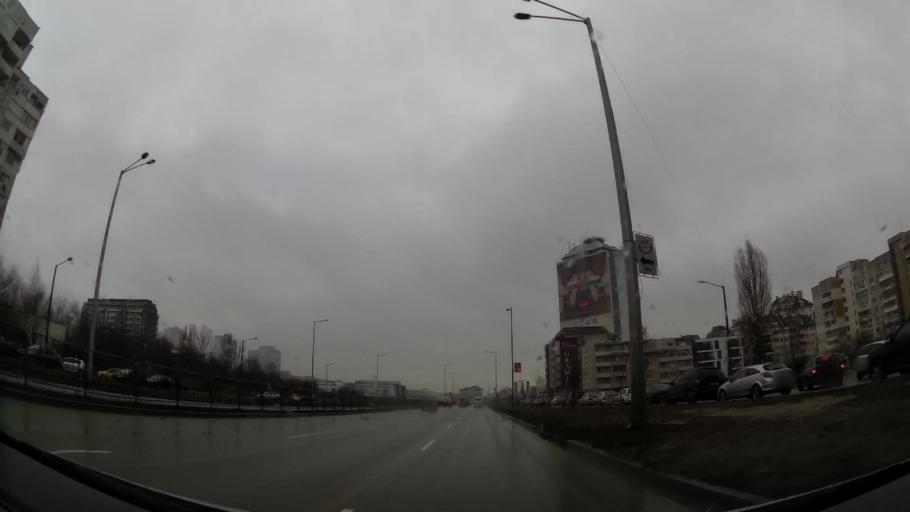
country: BG
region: Sofia-Capital
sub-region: Stolichna Obshtina
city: Sofia
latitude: 42.6331
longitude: 23.3732
